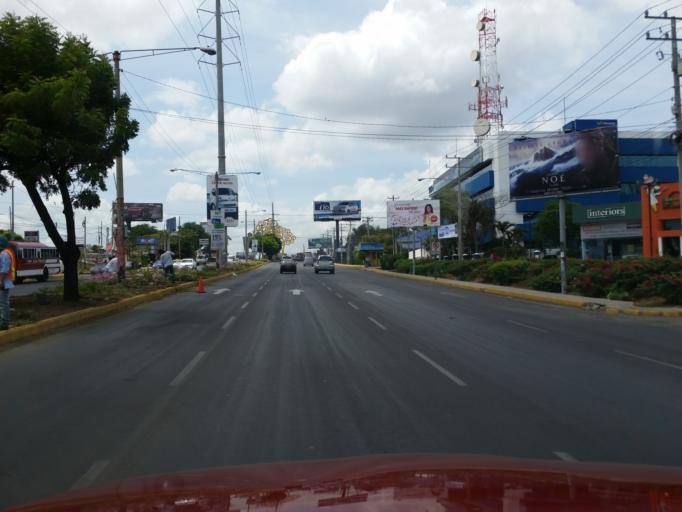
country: NI
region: Managua
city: Managua
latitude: 12.1087
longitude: -86.2511
